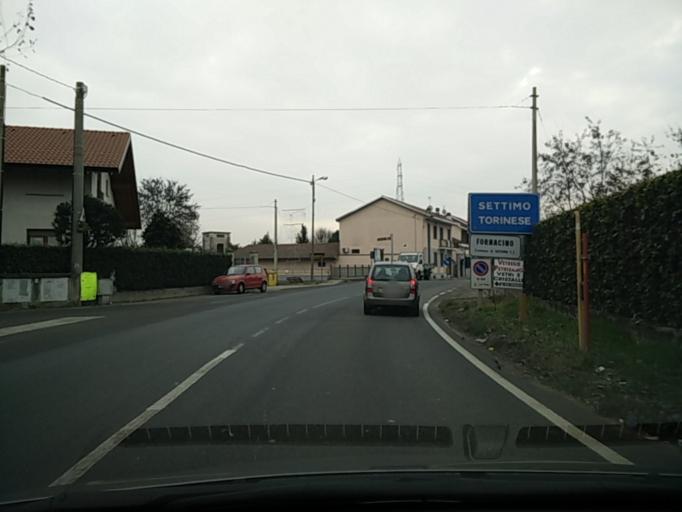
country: IT
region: Piedmont
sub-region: Provincia di Torino
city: Settimo Torinese
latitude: 45.1495
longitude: 7.7368
